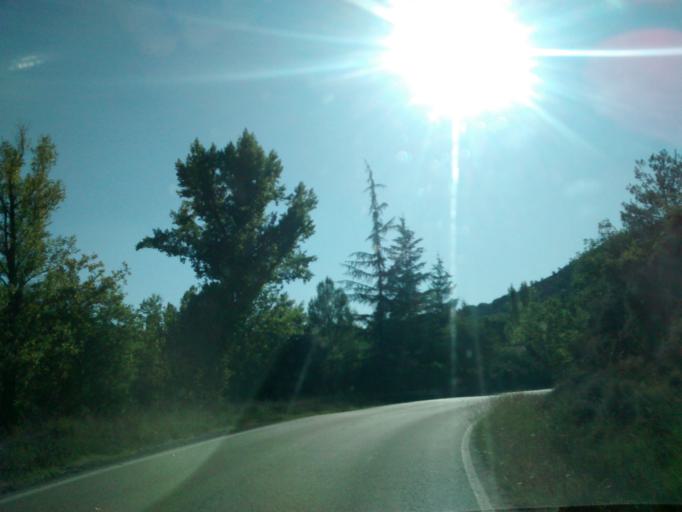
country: ES
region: Aragon
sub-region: Provincia de Huesca
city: Loarre
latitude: 42.4076
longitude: -0.6460
